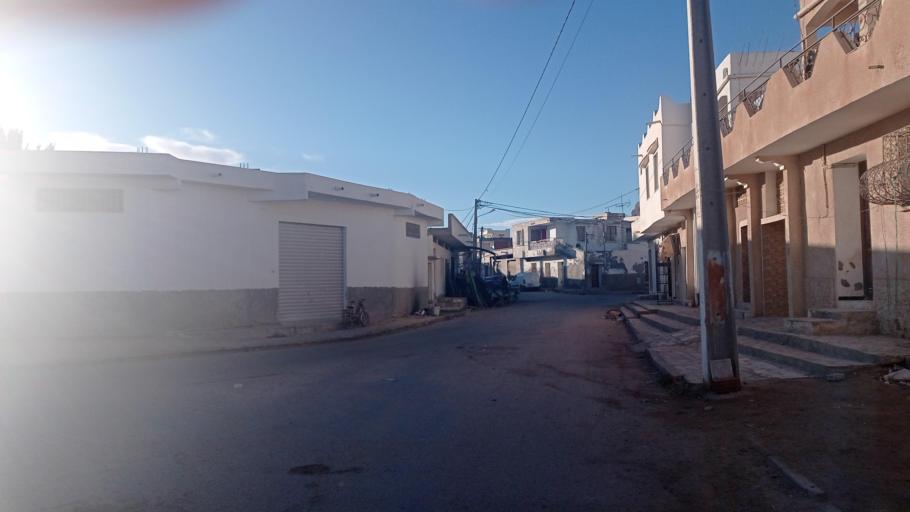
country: TN
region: Qabis
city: Gabes
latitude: 33.8433
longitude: 10.1197
